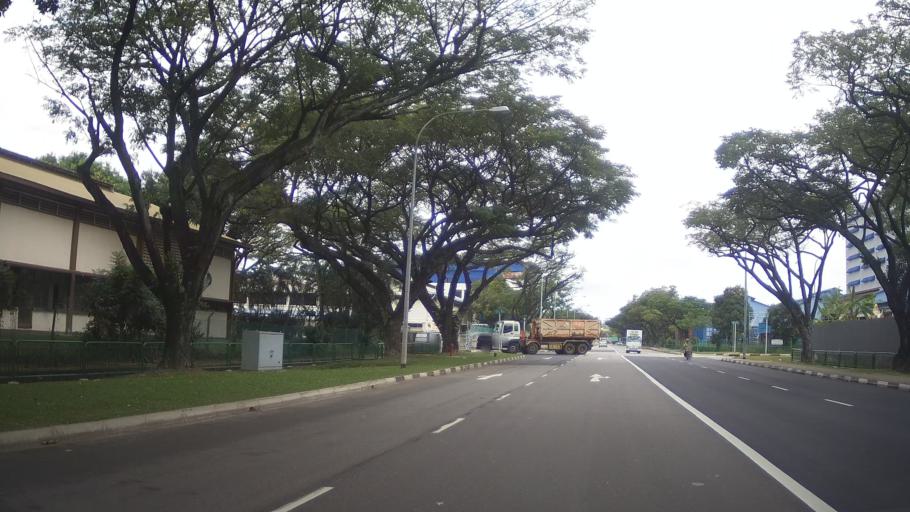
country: MY
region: Johor
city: Johor Bahru
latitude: 1.3165
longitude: 103.6704
